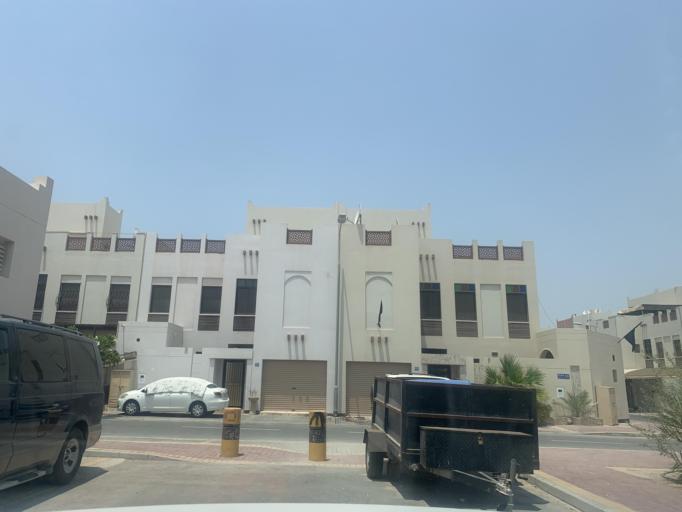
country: BH
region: Central Governorate
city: Madinat Hamad
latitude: 26.1454
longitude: 50.4621
